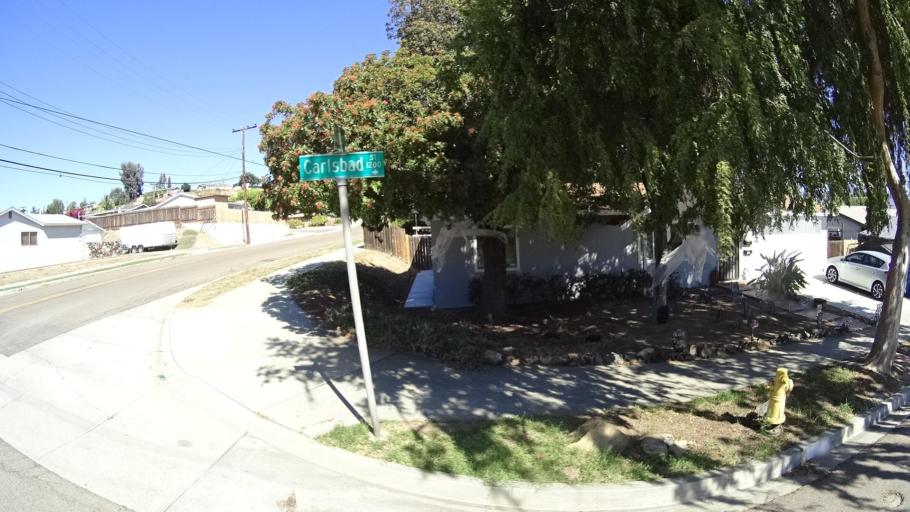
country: US
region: California
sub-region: San Diego County
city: La Presa
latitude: 32.7160
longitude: -117.0213
